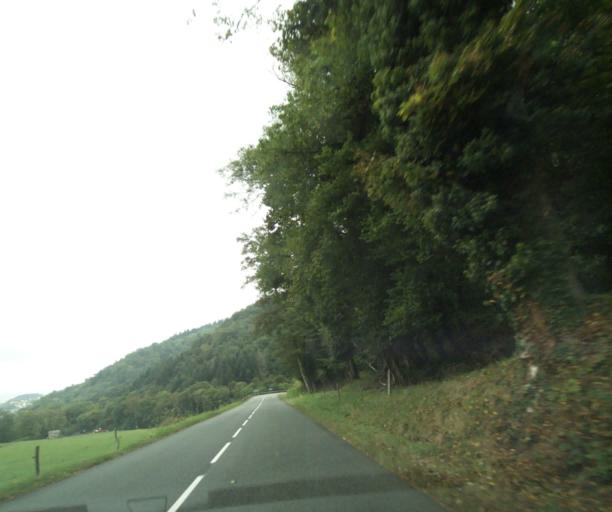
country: FR
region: Auvergne
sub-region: Departement du Puy-de-Dome
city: Royat
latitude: 45.7659
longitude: 3.0271
